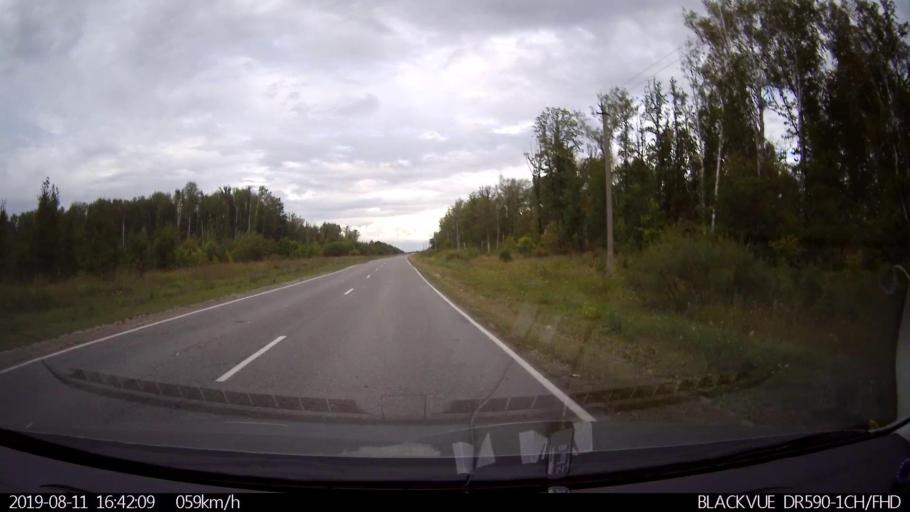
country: RU
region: Ulyanovsk
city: Mayna
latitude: 54.1582
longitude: 47.6599
